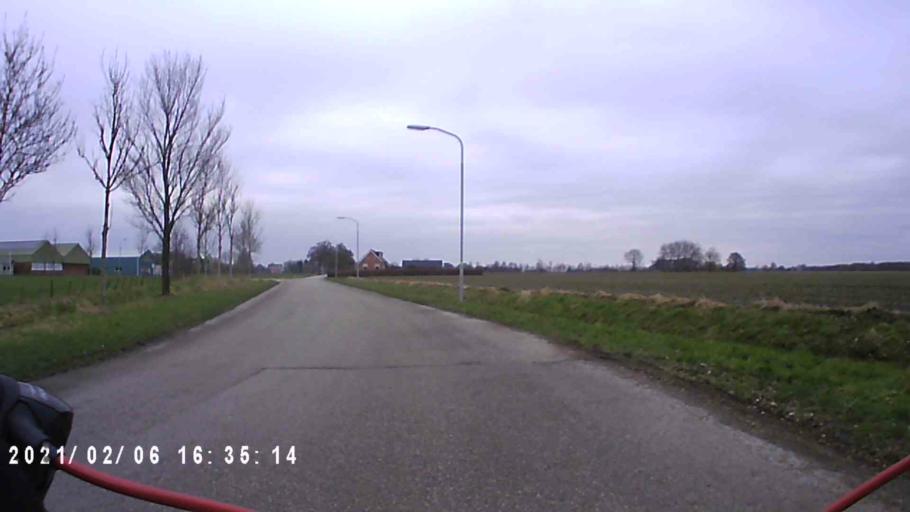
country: NL
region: Groningen
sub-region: Gemeente Bedum
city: Bedum
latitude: 53.4139
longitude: 6.6942
